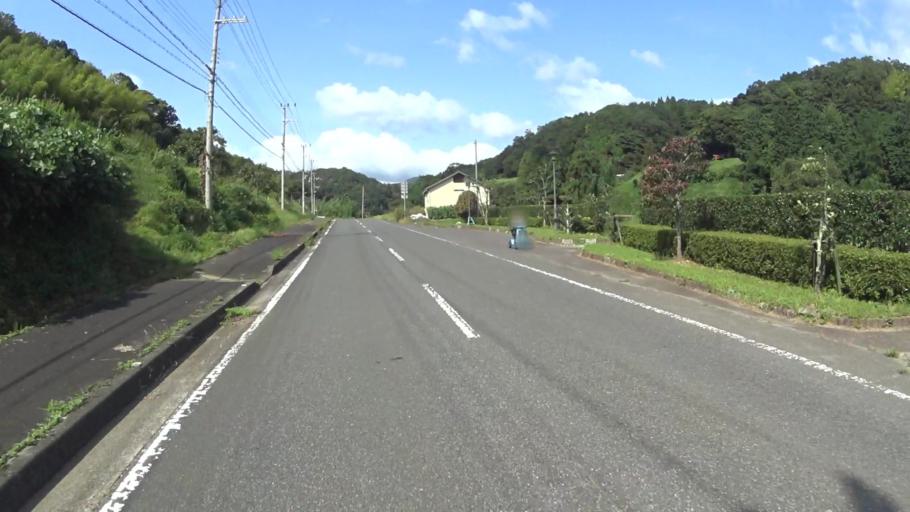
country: JP
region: Kyoto
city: Miyazu
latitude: 35.6263
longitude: 135.2426
